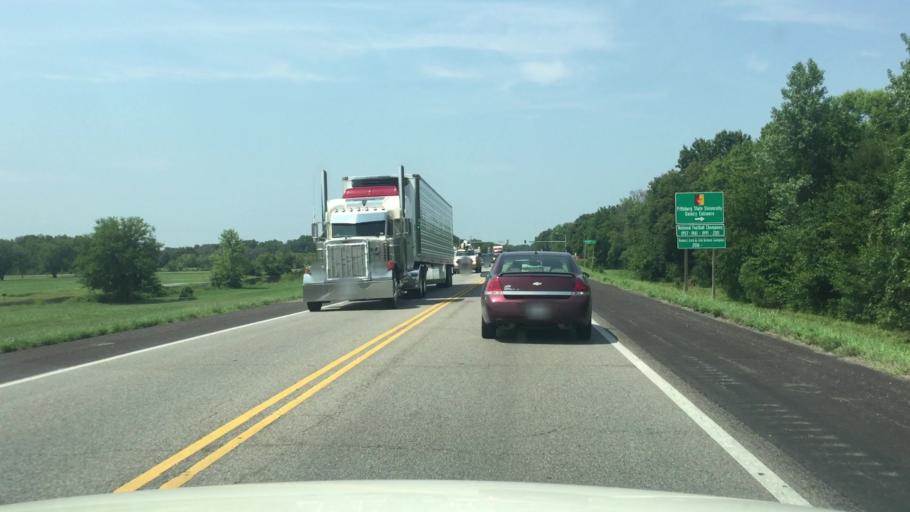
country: US
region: Kansas
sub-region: Crawford County
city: Pittsburg
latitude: 37.3939
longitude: -94.7177
